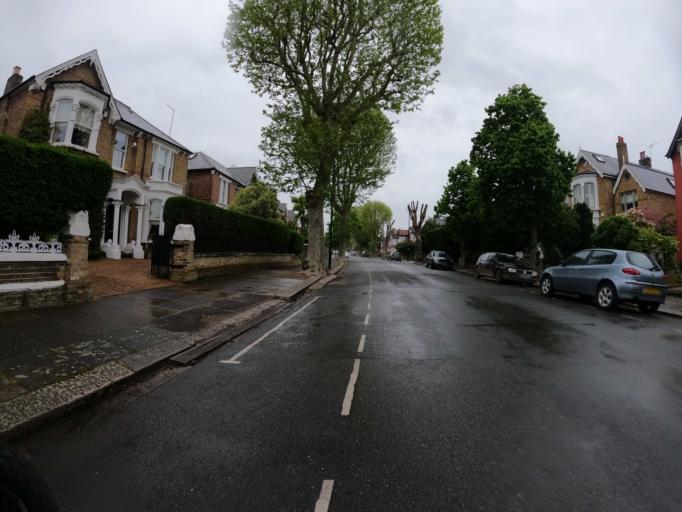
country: GB
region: England
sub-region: Greater London
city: Acton
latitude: 51.5123
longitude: -0.2752
